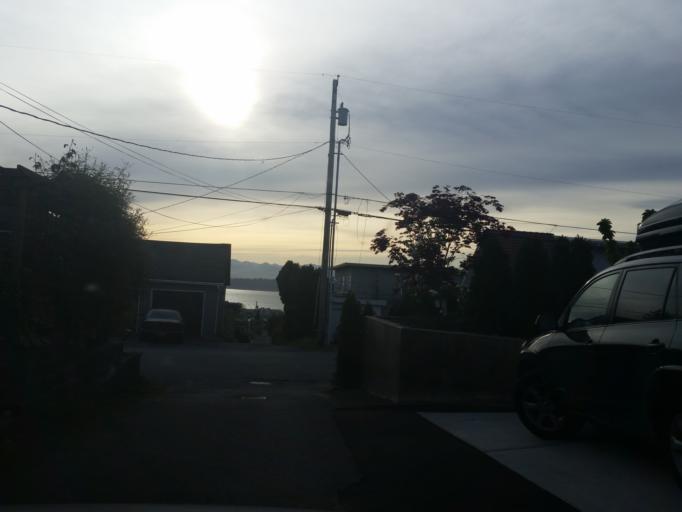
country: US
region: Washington
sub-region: Snohomish County
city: Edmonds
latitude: 47.8109
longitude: -122.3691
